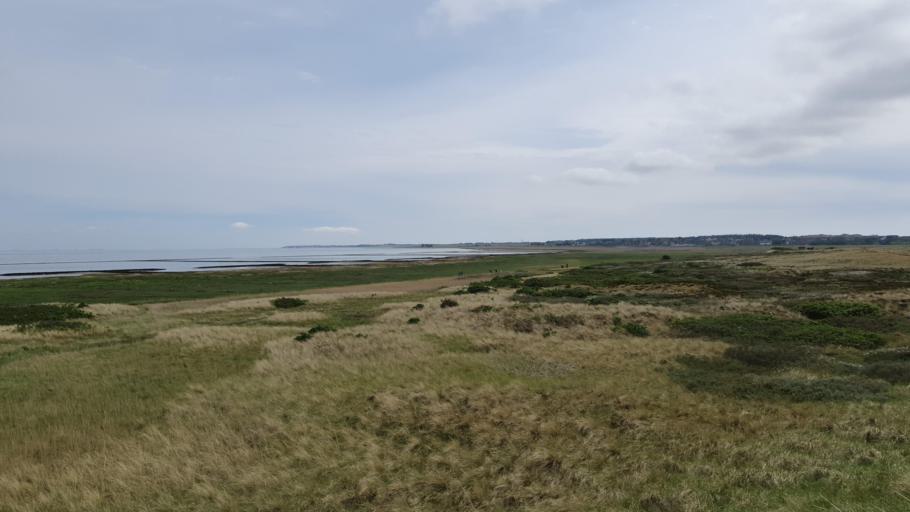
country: DE
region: Schleswig-Holstein
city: Norddorf
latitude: 54.6976
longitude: 8.3369
